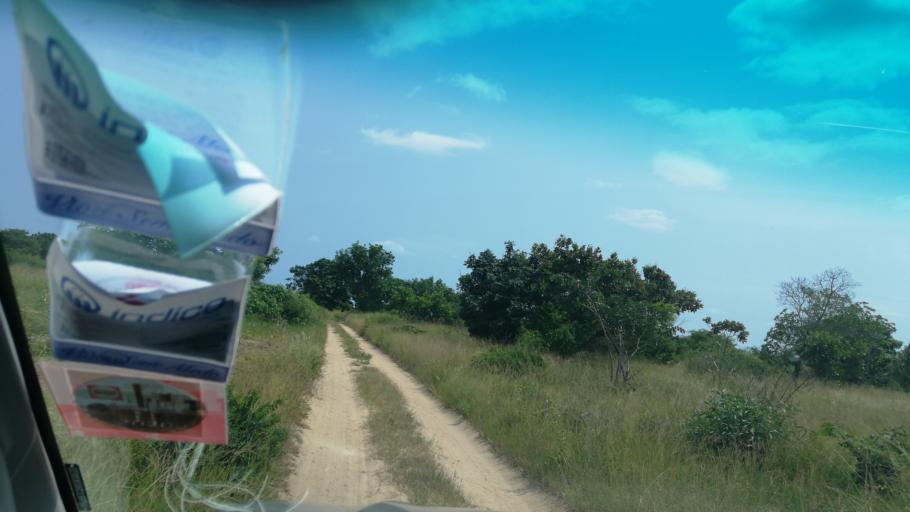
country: MZ
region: Maputo
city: Matola
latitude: -26.1102
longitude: 32.4217
